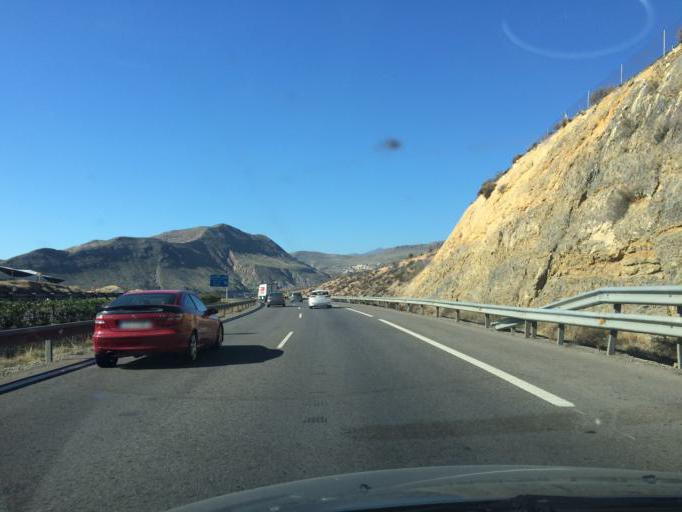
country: ES
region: Andalusia
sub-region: Provincia de Almeria
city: Aguadulce
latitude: 36.8275
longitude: -2.5850
